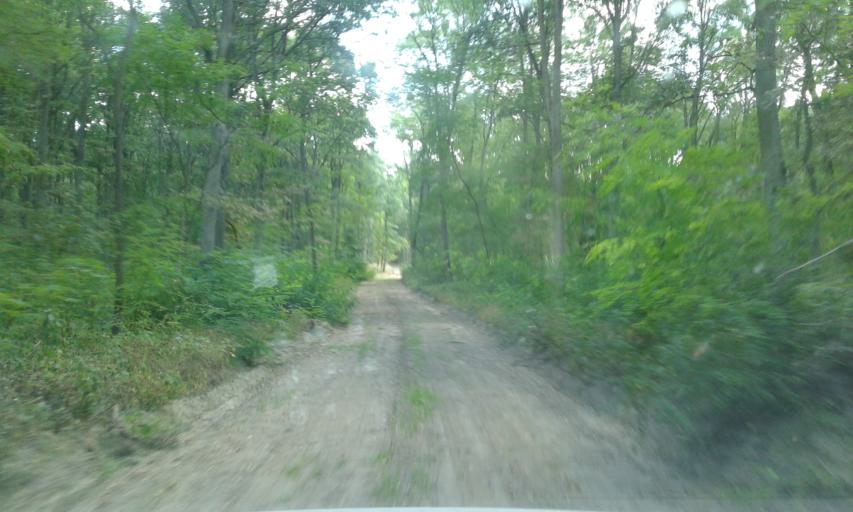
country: PL
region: West Pomeranian Voivodeship
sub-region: Powiat stargardzki
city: Dolice
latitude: 53.2359
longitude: 15.2416
